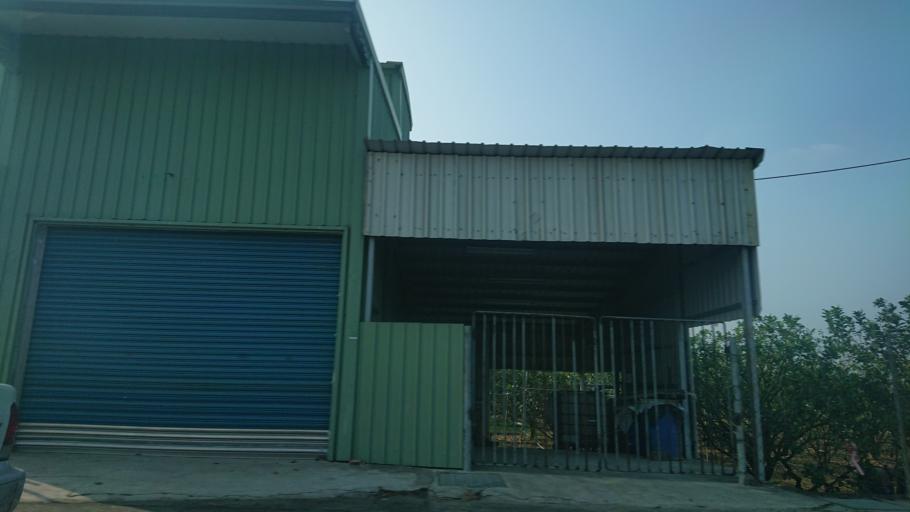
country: TW
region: Taiwan
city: Xinying
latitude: 23.2056
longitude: 120.2716
